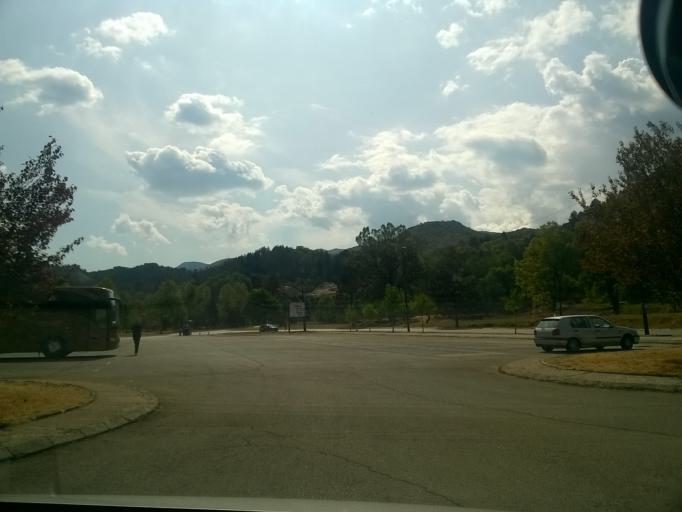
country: ME
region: Cetinje
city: Cetinje
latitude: 42.3860
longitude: 18.9237
